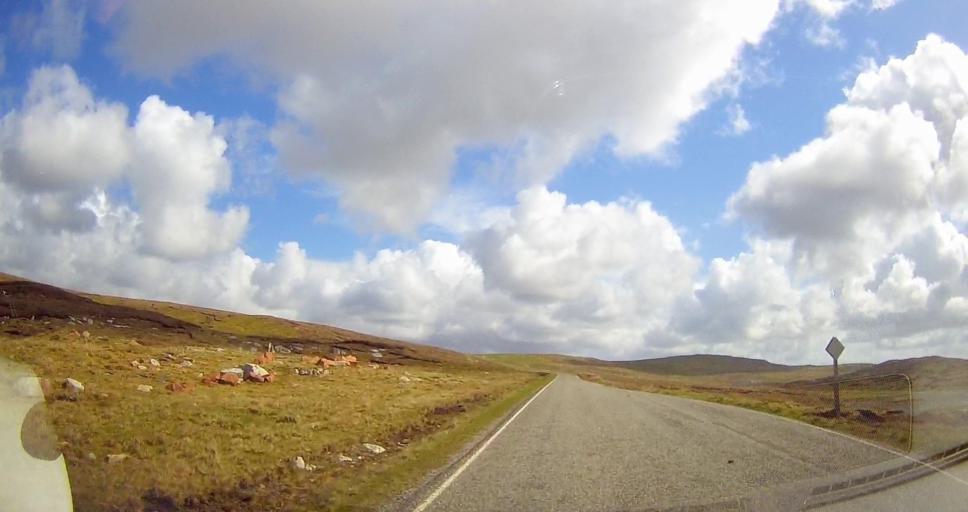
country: GB
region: Scotland
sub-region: Shetland Islands
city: Lerwick
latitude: 60.4981
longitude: -1.3969
